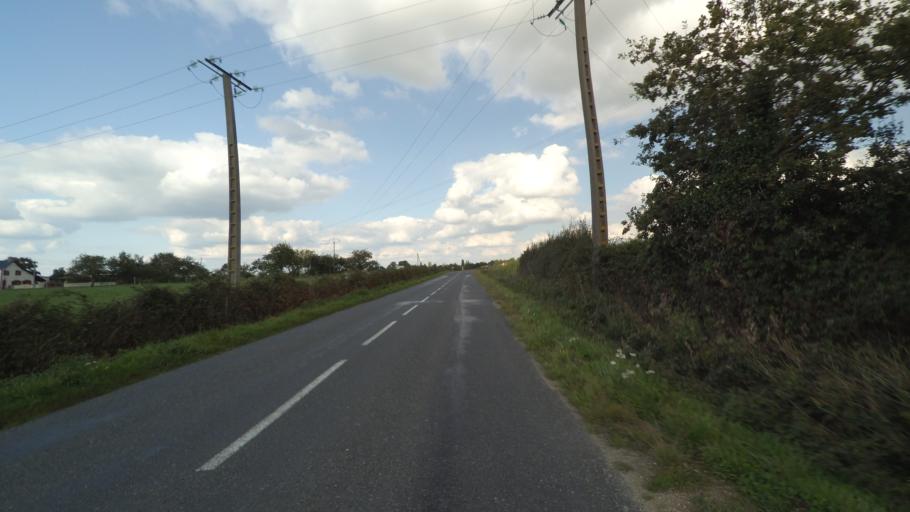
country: FR
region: Pays de la Loire
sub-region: Departement de la Loire-Atlantique
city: Vieillevigne
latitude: 46.9819
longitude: -1.4070
